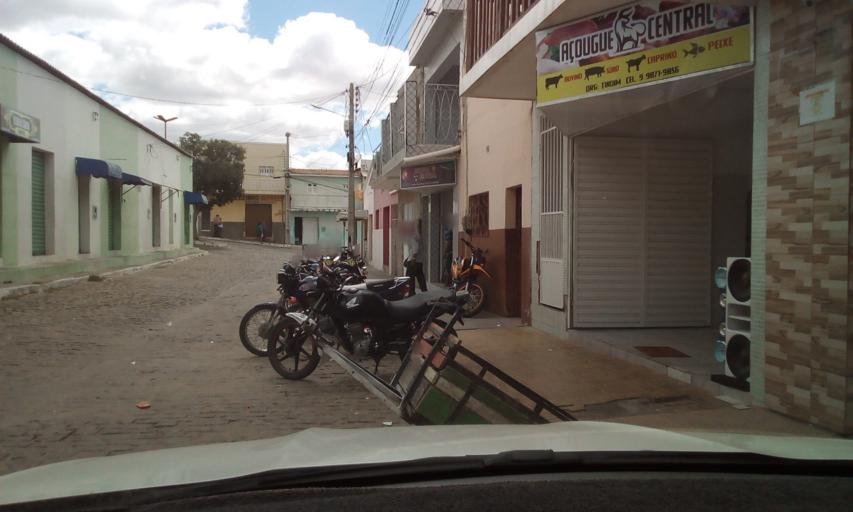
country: BR
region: Paraiba
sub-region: Picui
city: Picui
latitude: -6.5092
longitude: -36.3465
